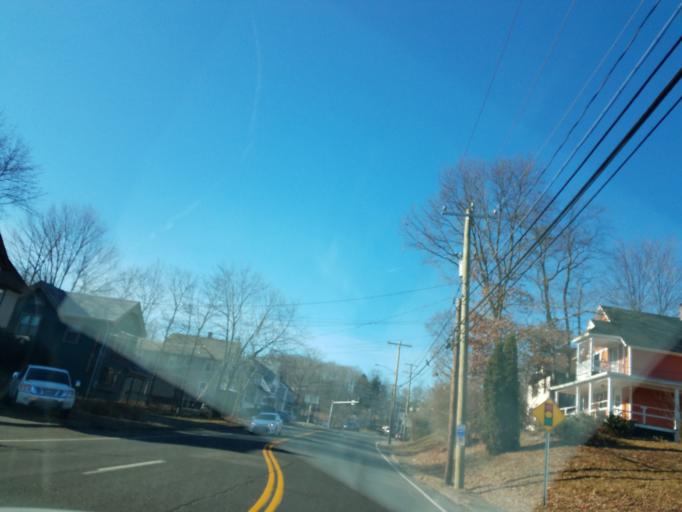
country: US
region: Connecticut
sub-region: New Haven County
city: Meriden
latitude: 41.5408
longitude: -72.8233
